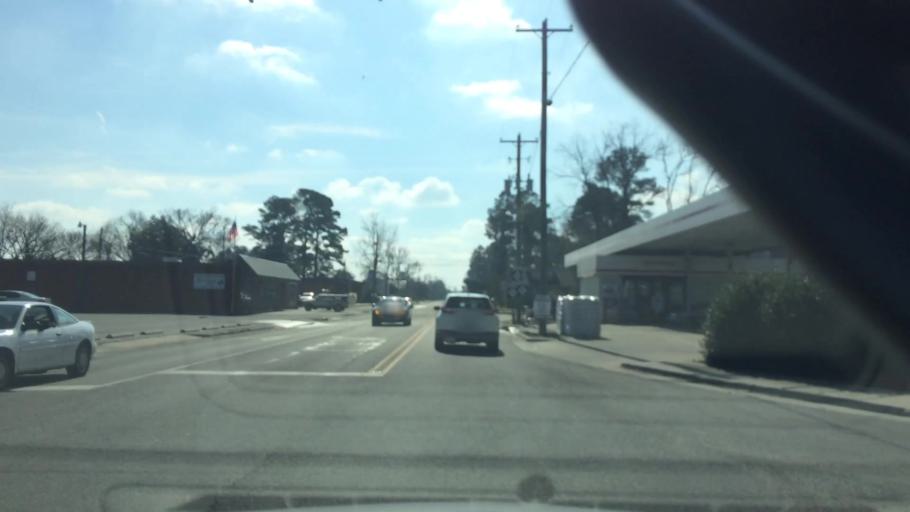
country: US
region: North Carolina
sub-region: Duplin County
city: Beulaville
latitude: 34.9237
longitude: -77.7737
